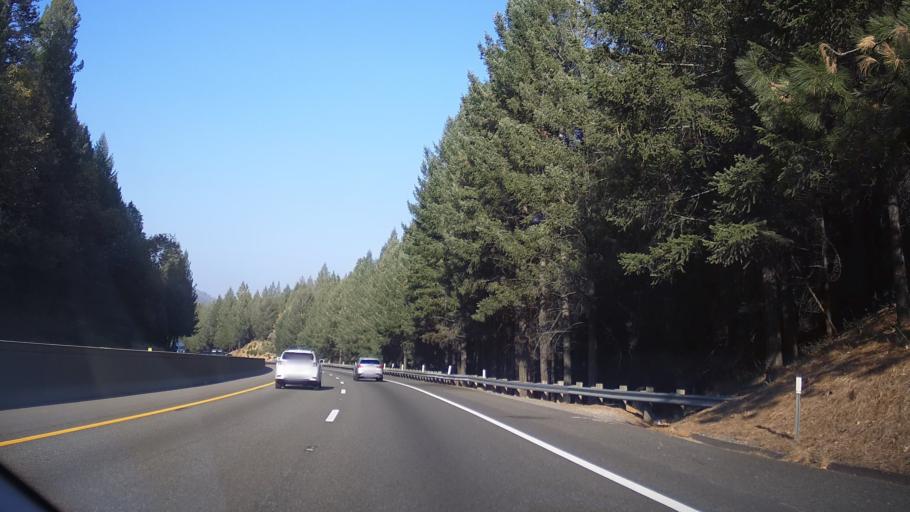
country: US
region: California
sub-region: Placer County
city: Colfax
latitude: 39.0659
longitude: -120.9648
